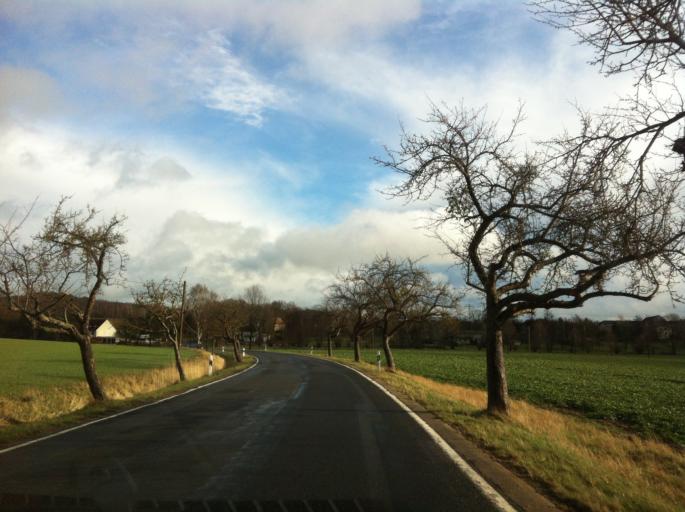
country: DE
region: Saxony
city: Hohburg
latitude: 51.4183
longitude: 12.7778
